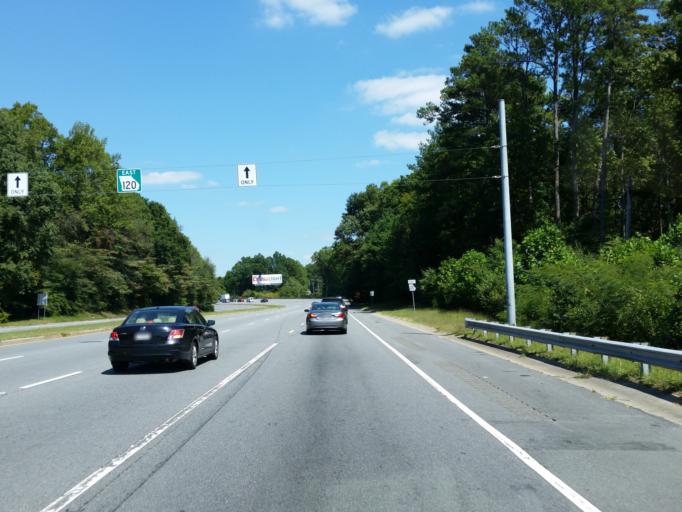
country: US
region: Georgia
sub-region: Cobb County
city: Marietta
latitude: 33.9423
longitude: -84.5018
